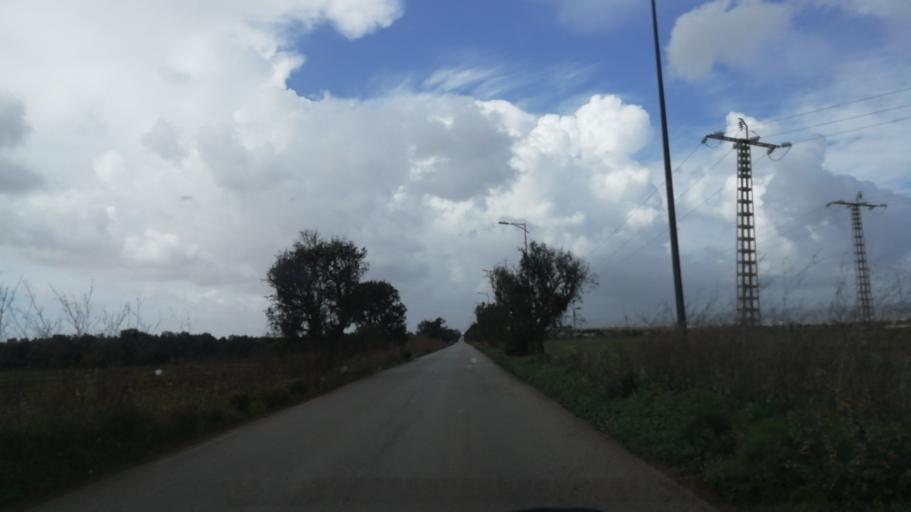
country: DZ
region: Oran
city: Sidi ech Chahmi
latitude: 35.6226
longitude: -0.5534
